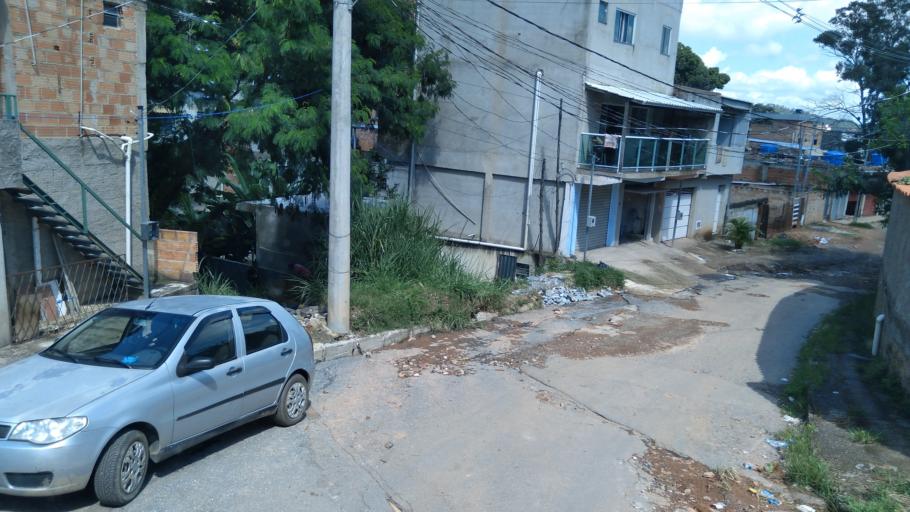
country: BR
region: Minas Gerais
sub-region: Santa Luzia
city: Santa Luzia
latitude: -19.8319
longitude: -43.8905
